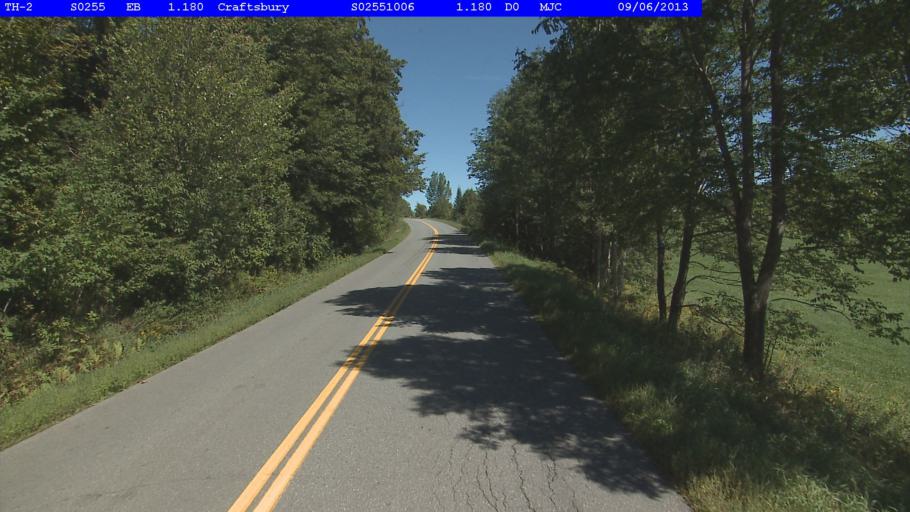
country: US
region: Vermont
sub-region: Caledonia County
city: Hardwick
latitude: 44.6345
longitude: -72.3476
